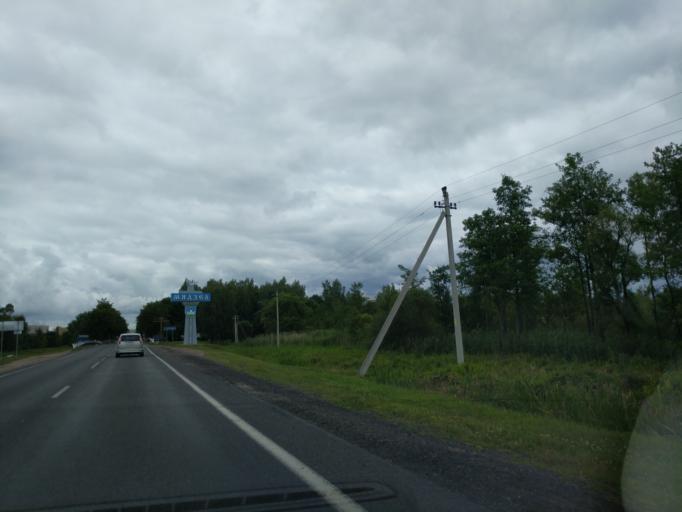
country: BY
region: Minsk
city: Myadzyel
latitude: 54.8632
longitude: 26.9330
